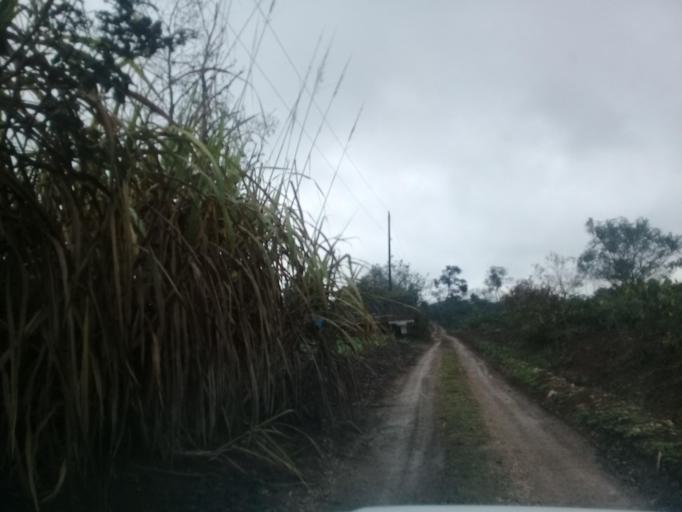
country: MX
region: Veracruz
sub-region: Amatlan de los Reyes
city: Centro de Readaptacion Social
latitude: 18.8171
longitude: -96.9406
